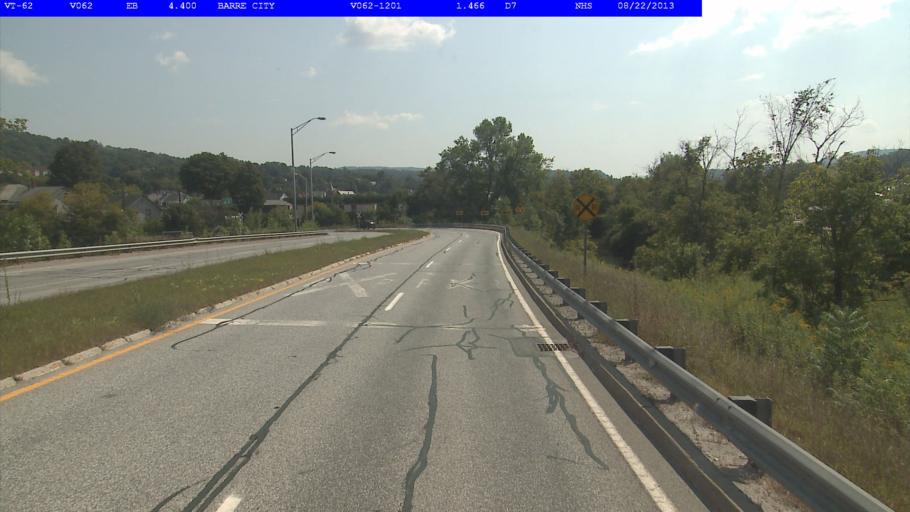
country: US
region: Vermont
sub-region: Washington County
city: Barre
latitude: 44.2023
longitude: -72.5099
